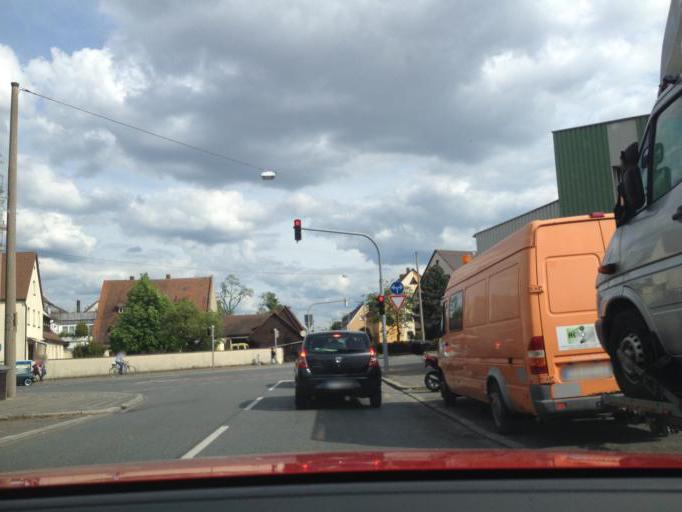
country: DE
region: Bavaria
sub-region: Regierungsbezirk Mittelfranken
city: Grossreuth bei Schweinau
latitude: 49.4554
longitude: 11.0163
